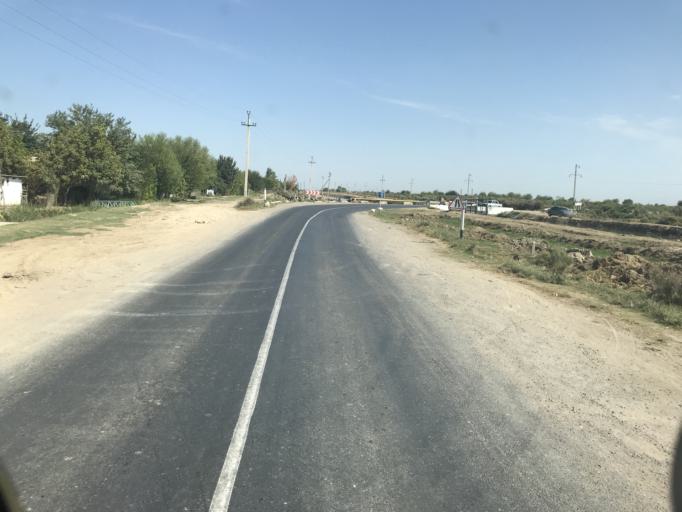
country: KZ
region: Ongtustik Qazaqstan
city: Myrzakent
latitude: 40.7156
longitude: 68.5338
